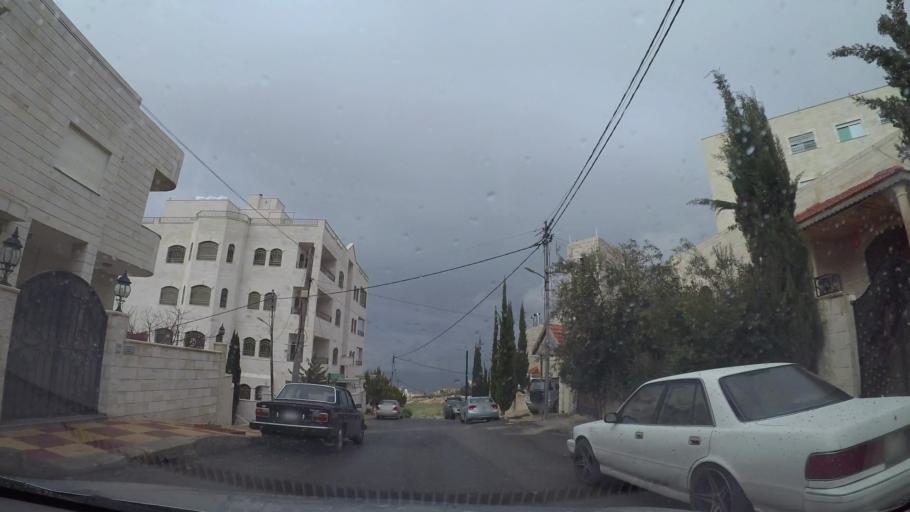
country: JO
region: Amman
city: Al Jubayhah
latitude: 32.0357
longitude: 35.8433
